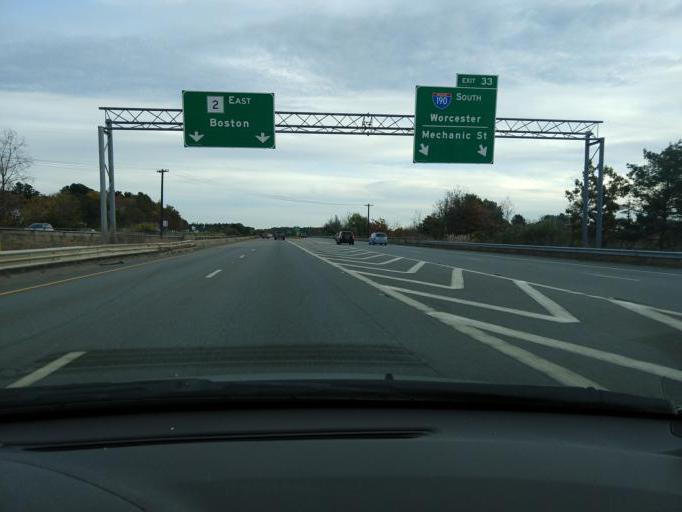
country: US
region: Massachusetts
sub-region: Worcester County
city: Leominster
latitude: 42.5295
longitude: -71.7348
